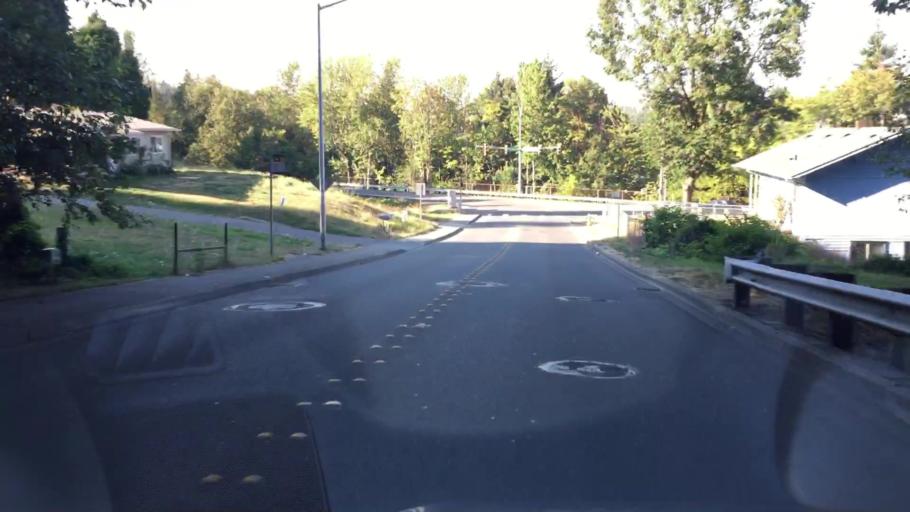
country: US
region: Washington
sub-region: King County
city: Tukwila
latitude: 47.4604
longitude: -122.2679
